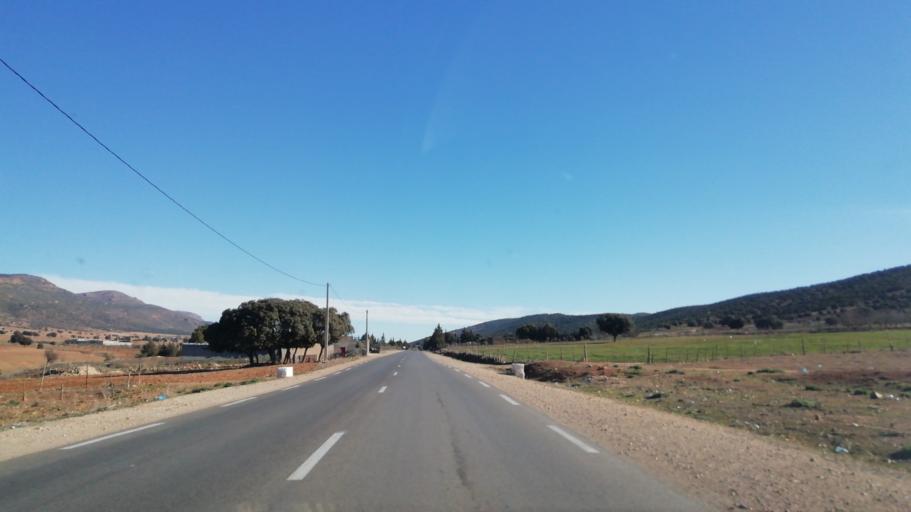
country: DZ
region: Tlemcen
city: Sebdou
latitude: 34.6790
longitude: -1.2605
